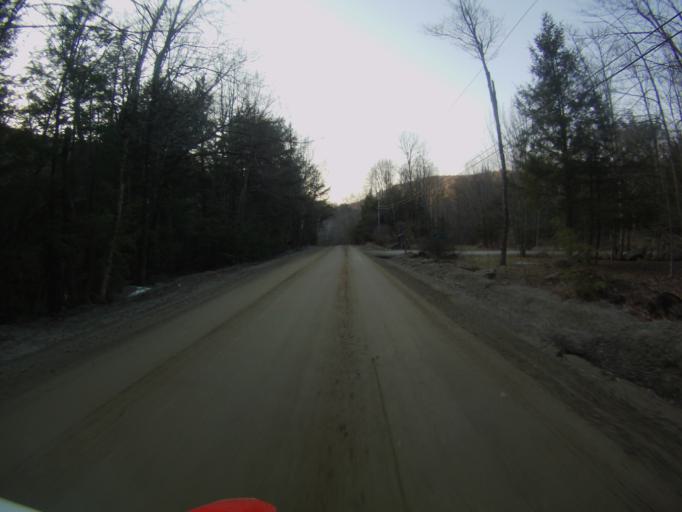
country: US
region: Vermont
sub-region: Addison County
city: Bristol
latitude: 44.0721
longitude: -73.0591
